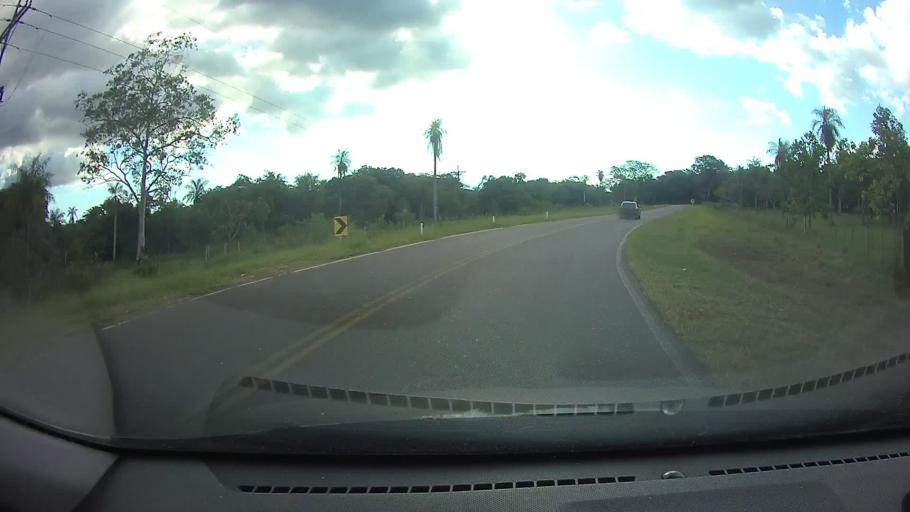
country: PY
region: Cordillera
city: Atyra
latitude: -25.2848
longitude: -57.1961
